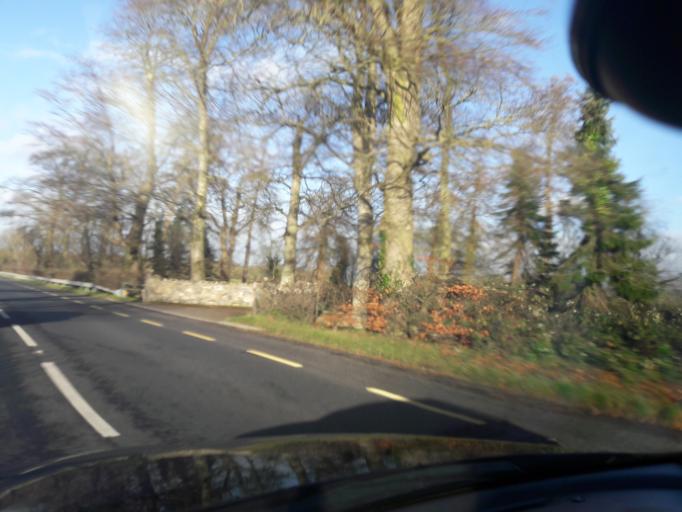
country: IE
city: Kentstown
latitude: 53.5977
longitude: -6.4682
